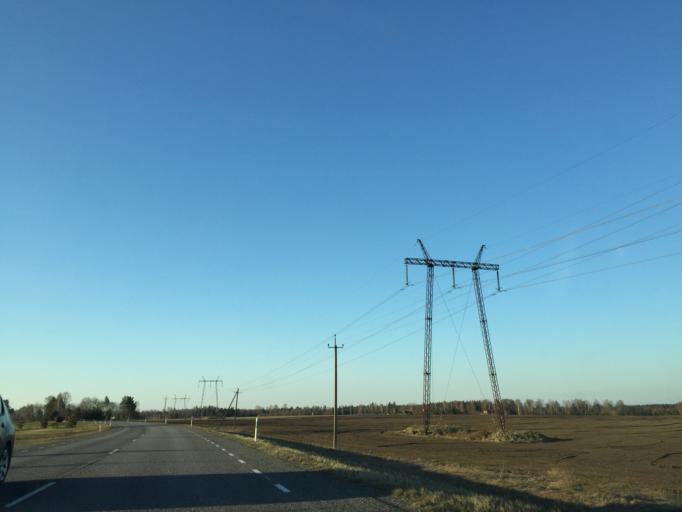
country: EE
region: Ida-Virumaa
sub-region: Johvi vald
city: Johvi
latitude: 59.3100
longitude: 27.4981
